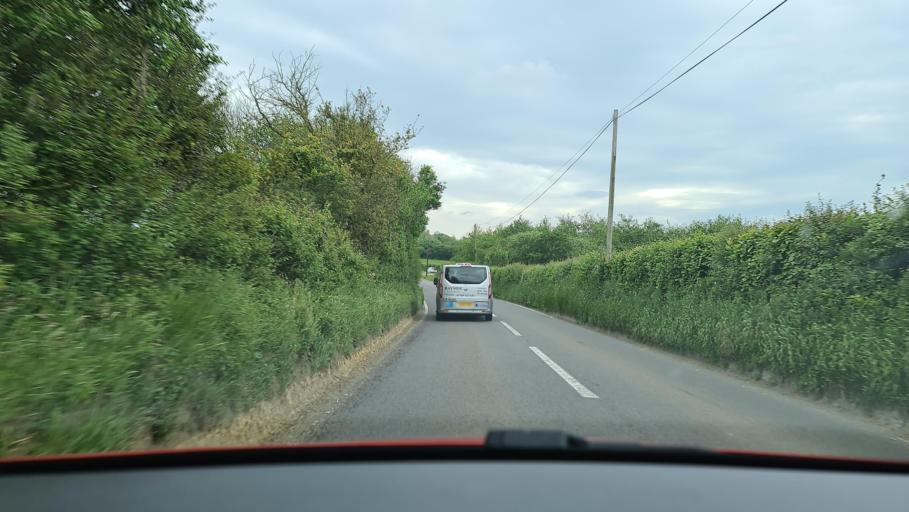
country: GB
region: England
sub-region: Cornwall
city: Poundstock
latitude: 50.7926
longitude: -4.5320
